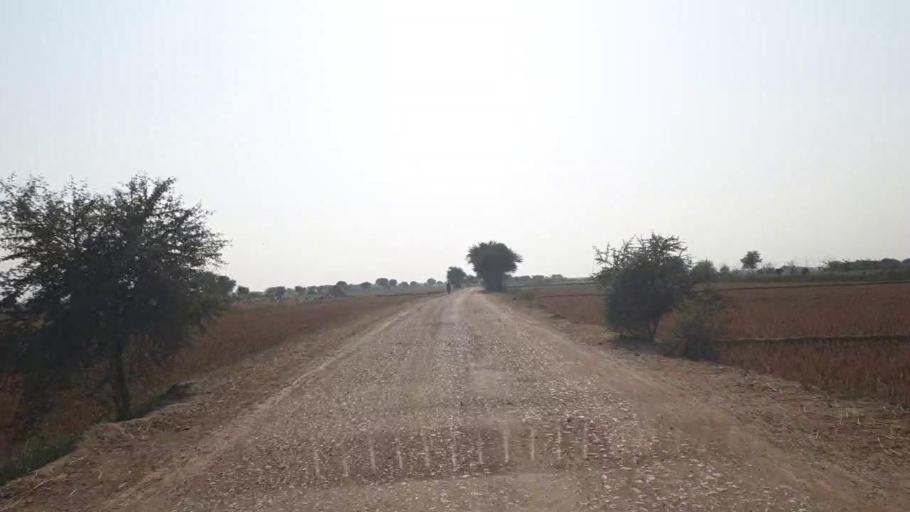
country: PK
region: Sindh
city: Matli
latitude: 24.9452
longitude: 68.6821
